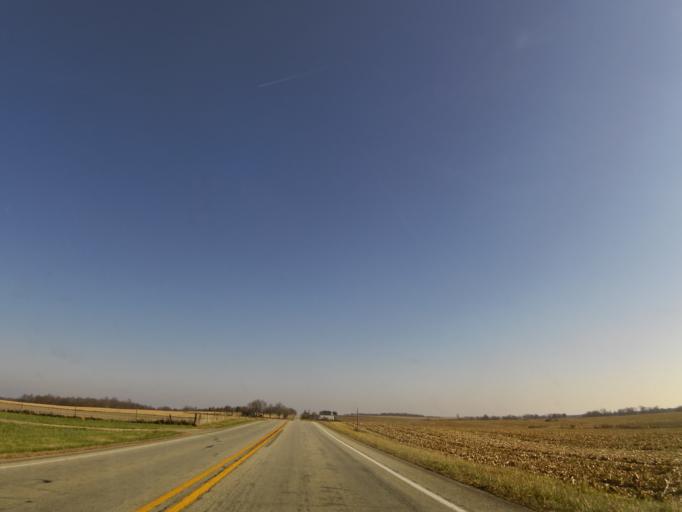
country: US
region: Indiana
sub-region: Fayette County
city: Connersville
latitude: 39.6287
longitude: -85.2579
